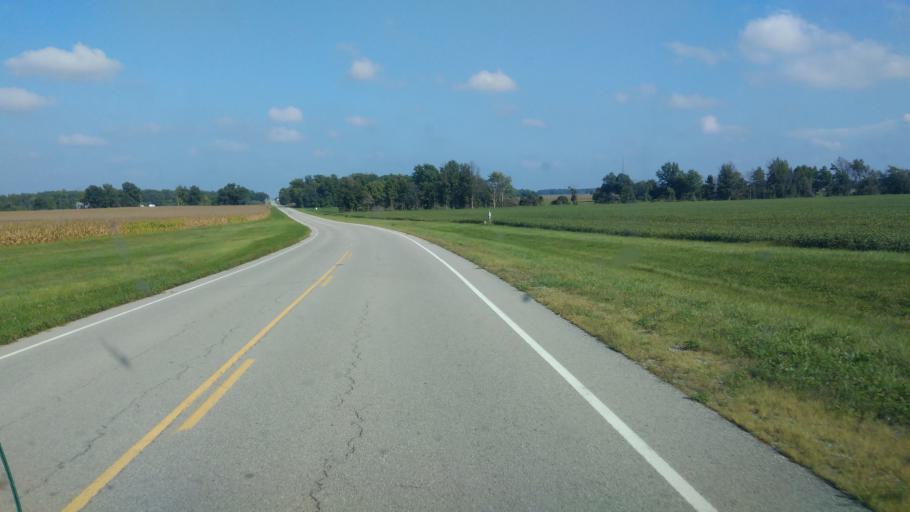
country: US
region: Ohio
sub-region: Hancock County
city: Arlington
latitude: 40.8340
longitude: -83.6415
